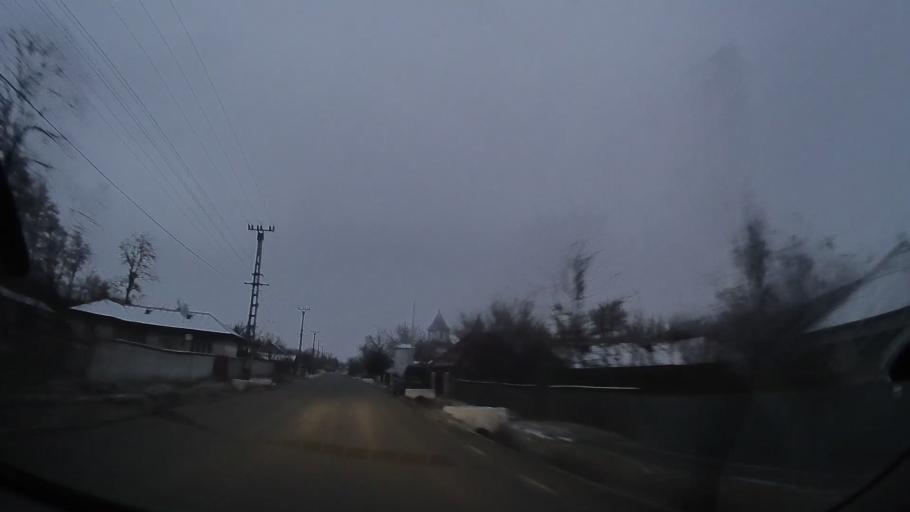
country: RO
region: Vaslui
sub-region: Comuna Vutcani
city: Vutcani
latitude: 46.4124
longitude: 27.9954
